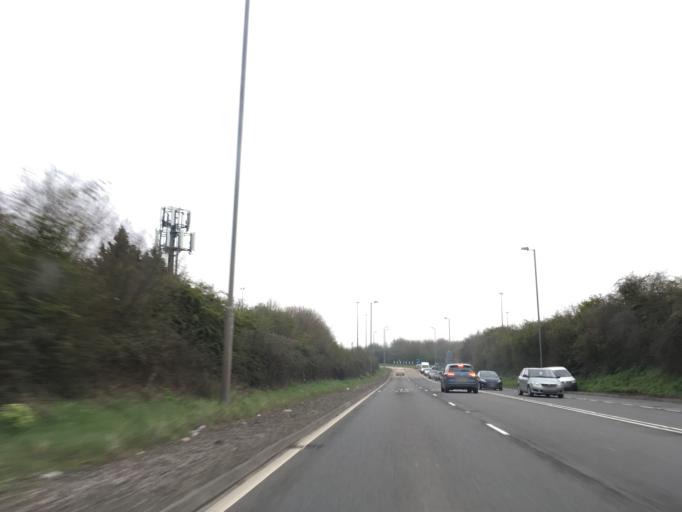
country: GB
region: Wales
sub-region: Monmouthshire
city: Chepstow
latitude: 51.6233
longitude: -2.6750
